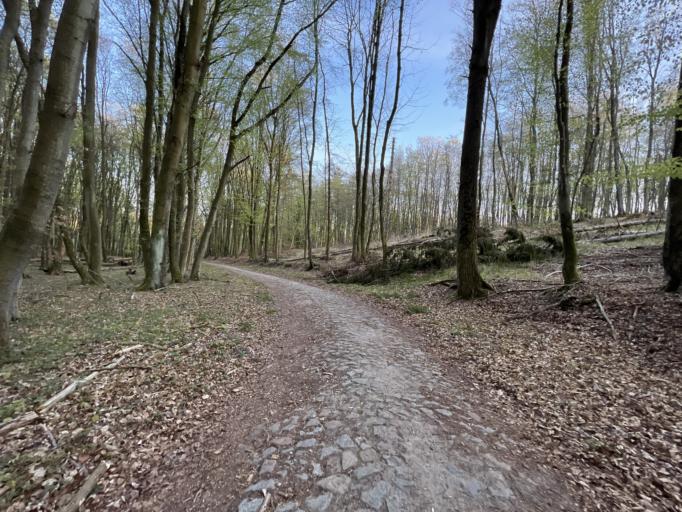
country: DE
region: Mecklenburg-Vorpommern
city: Sassnitz
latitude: 54.5300
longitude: 13.6548
